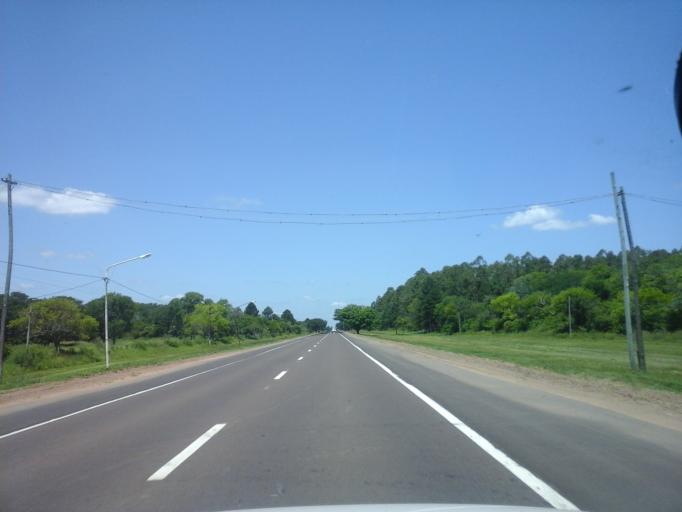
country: AR
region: Corrientes
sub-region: Departamento de San Cosme
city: San Cosme
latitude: -27.3678
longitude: -58.3888
